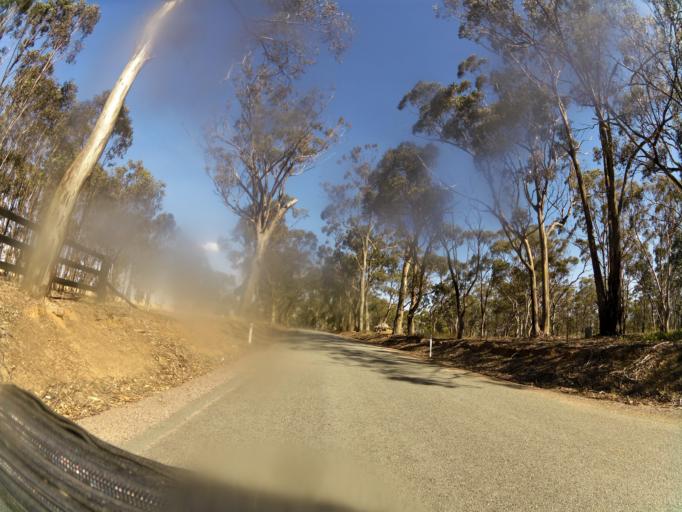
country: AU
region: Victoria
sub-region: Campaspe
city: Kyabram
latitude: -36.8775
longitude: 145.0859
